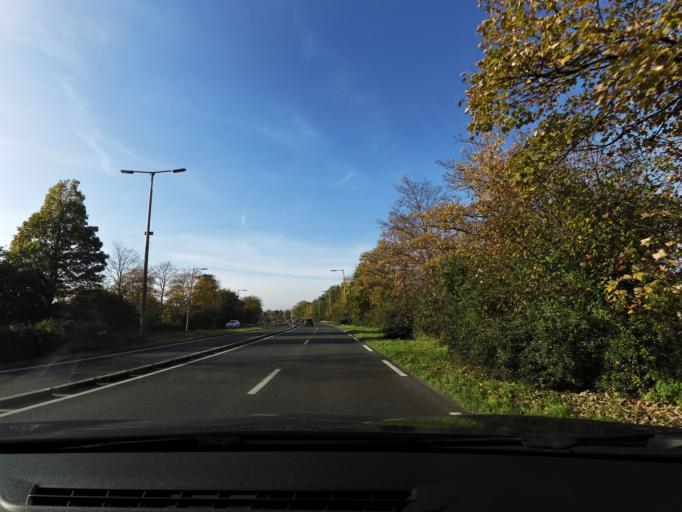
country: NL
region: South Holland
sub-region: Gemeente Ridderkerk
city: Ridderkerk
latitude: 51.8851
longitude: 4.5847
